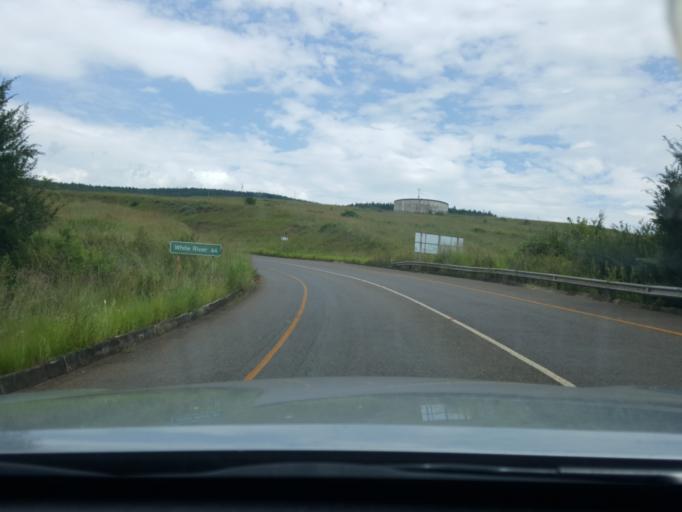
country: ZA
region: Mpumalanga
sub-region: Ehlanzeni District
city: Graksop
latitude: -25.1018
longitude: 30.7835
